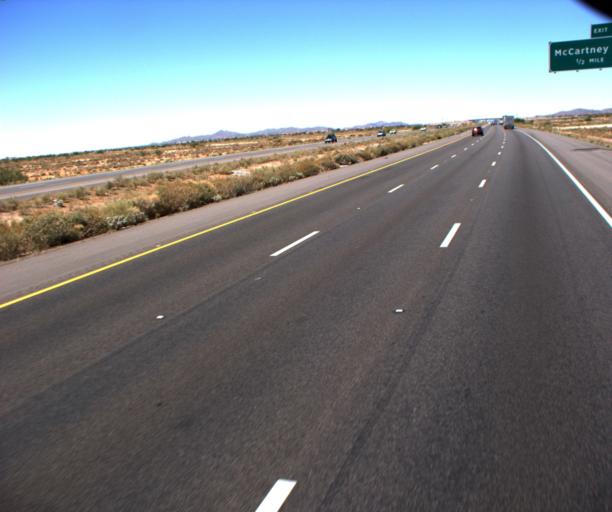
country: US
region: Arizona
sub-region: Pinal County
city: Casa Grande
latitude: 32.9275
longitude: -111.6920
